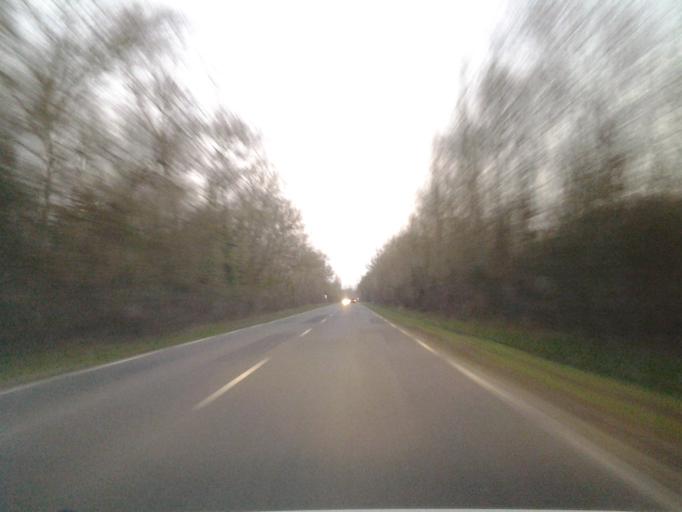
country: FR
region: Pays de la Loire
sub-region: Departement de la Vendee
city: Saint-Gervais
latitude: 46.8925
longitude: -1.9797
